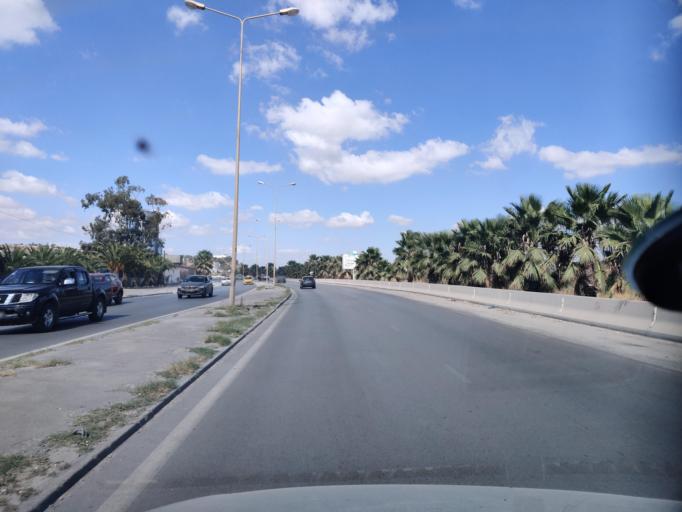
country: TN
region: Bin 'Arus
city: Ben Arous
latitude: 36.7801
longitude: 10.2032
